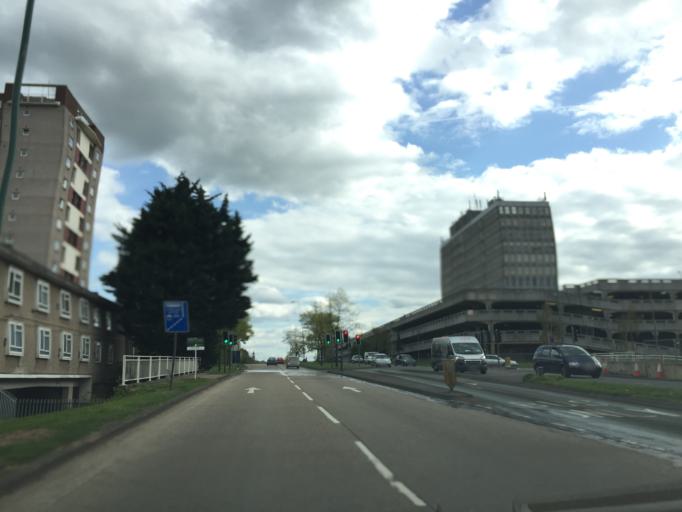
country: GB
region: England
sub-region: Essex
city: Harlow
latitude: 51.7720
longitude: 0.0960
